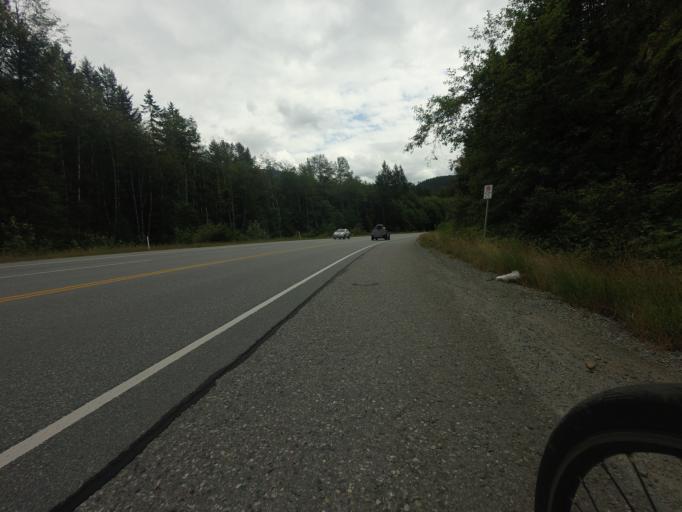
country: CA
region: British Columbia
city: Whistler
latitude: 49.8140
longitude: -123.1231
